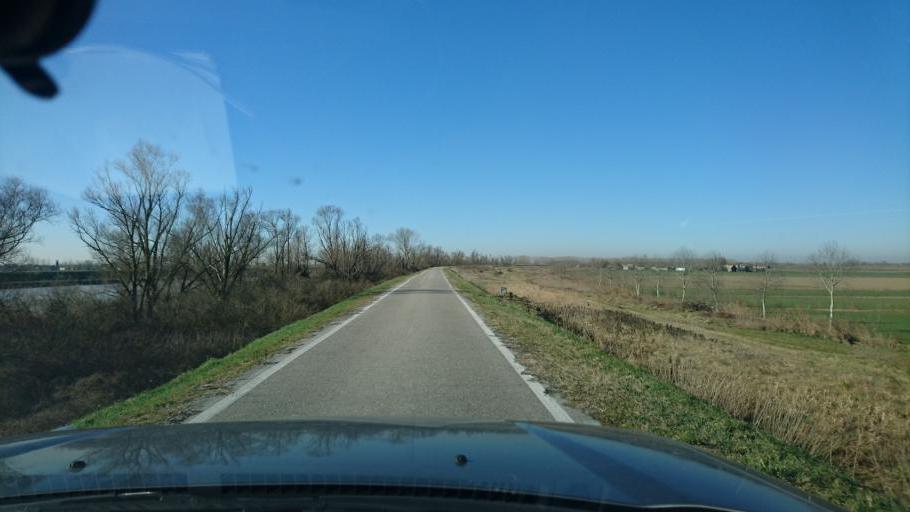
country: IT
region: Emilia-Romagna
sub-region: Provincia di Ferrara
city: Mesola
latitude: 44.9268
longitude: 12.2018
